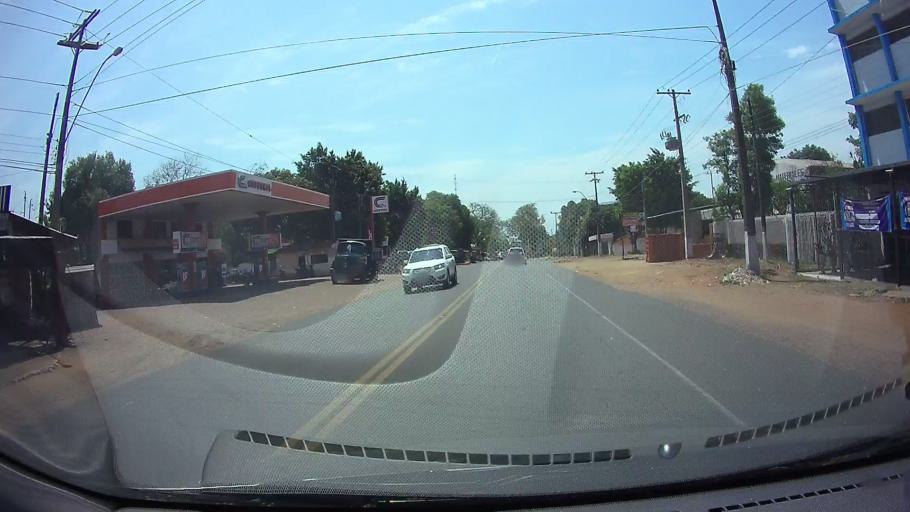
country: PY
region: Central
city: Capiata
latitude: -25.4082
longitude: -57.4608
